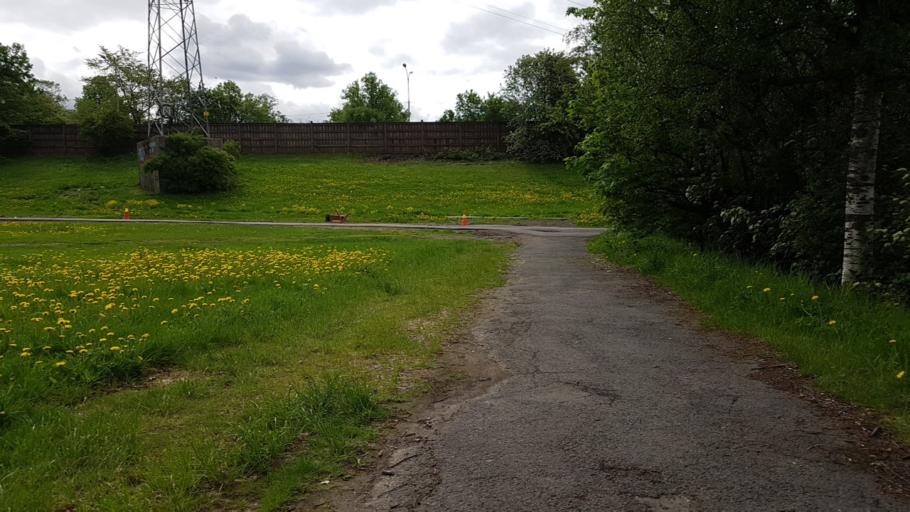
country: NO
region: Oslo
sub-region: Oslo
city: Oslo
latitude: 59.9418
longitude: 10.7993
